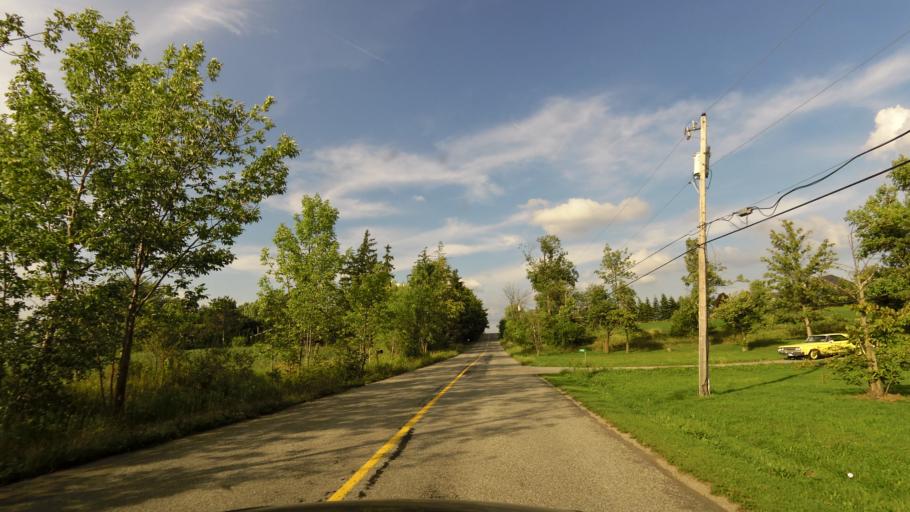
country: CA
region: Ontario
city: Burlington
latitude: 43.3825
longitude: -79.8681
